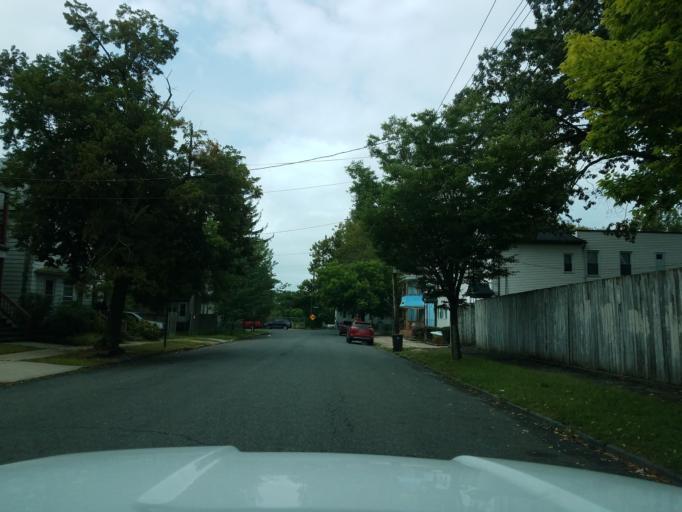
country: US
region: Connecticut
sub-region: New Haven County
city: West Haven
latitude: 41.2852
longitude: -72.9311
